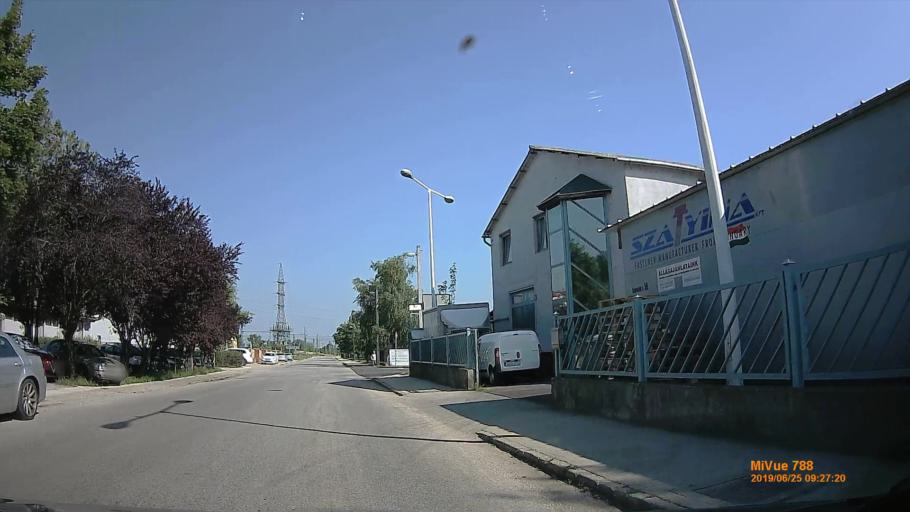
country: HU
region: Komarom-Esztergom
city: Esztergom
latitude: 47.7719
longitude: 18.7451
